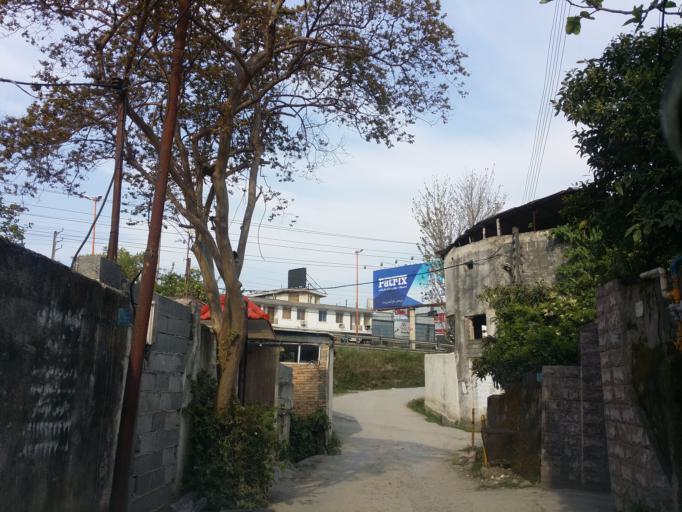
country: IR
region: Mazandaran
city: Chalus
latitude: 36.6856
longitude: 51.3977
